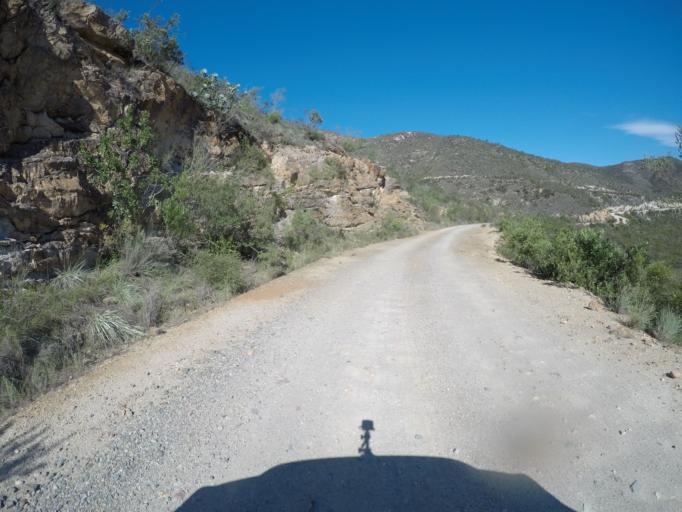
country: ZA
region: Eastern Cape
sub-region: Cacadu District Municipality
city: Kareedouw
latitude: -33.6531
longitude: 24.5028
